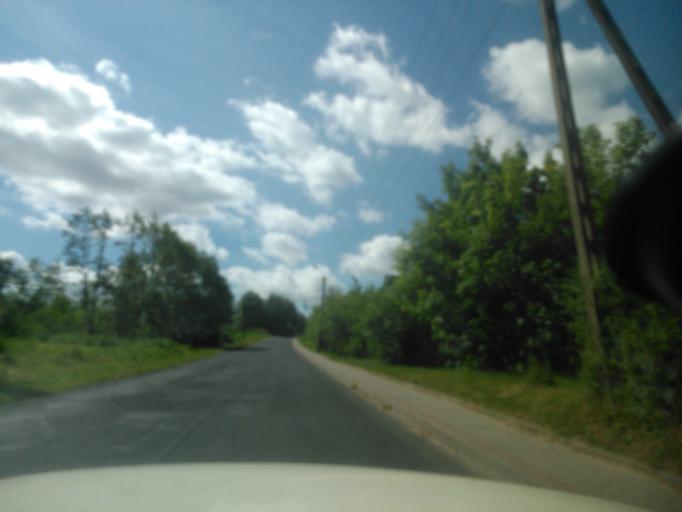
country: PL
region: Kujawsko-Pomorskie
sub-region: Powiat golubsko-dobrzynski
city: Ciechocin
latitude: 53.0596
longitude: 18.9261
